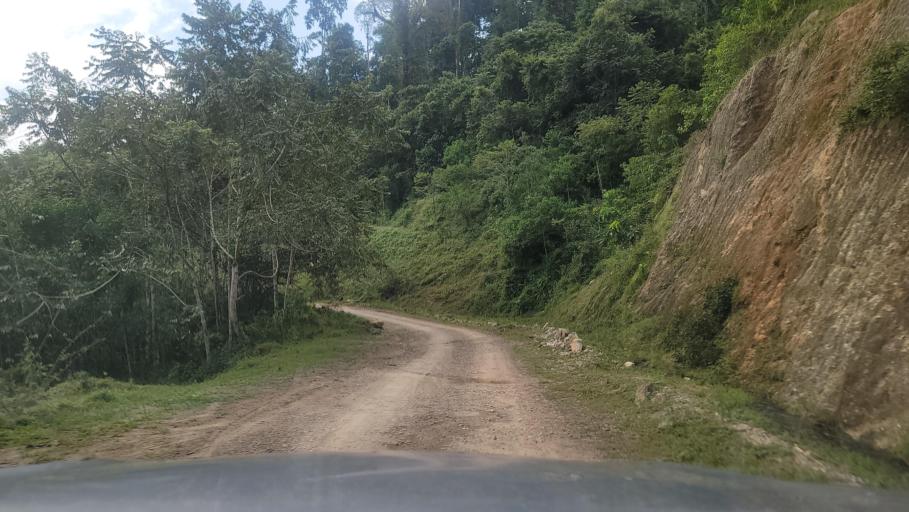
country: ET
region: Southern Nations, Nationalities, and People's Region
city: Bonga
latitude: 7.6054
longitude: 36.1986
